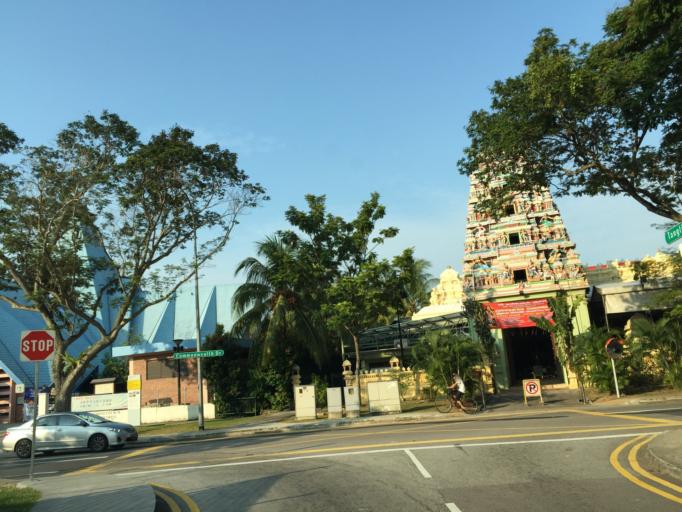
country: SG
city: Singapore
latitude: 1.2962
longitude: 103.7988
